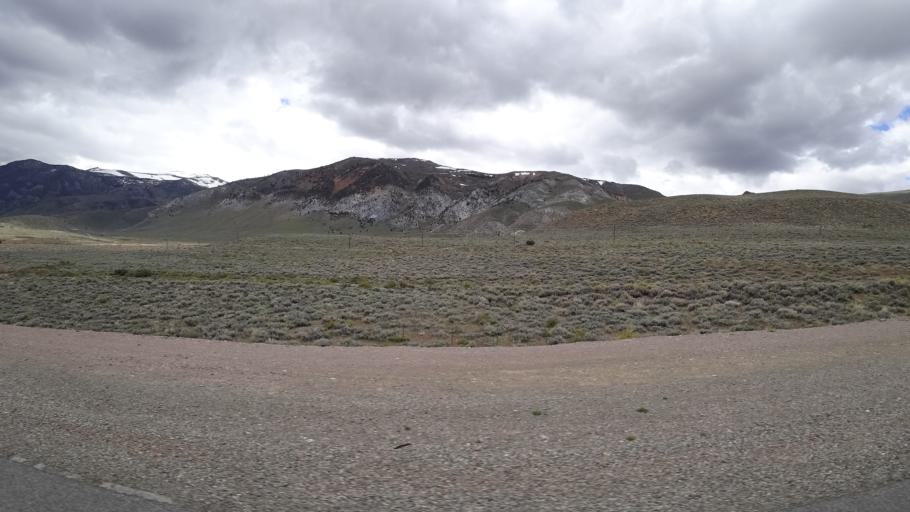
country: US
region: California
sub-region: Mono County
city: Bridgeport
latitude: 38.0557
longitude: -119.1660
